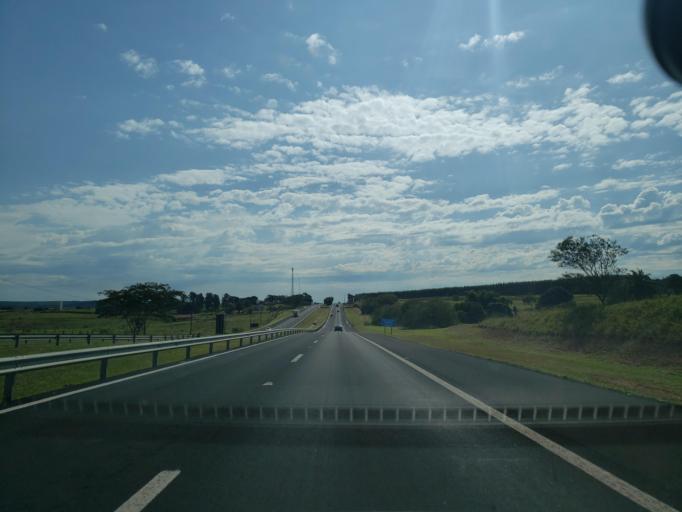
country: BR
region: Sao Paulo
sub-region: Pirajui
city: Pirajui
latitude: -22.0035
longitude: -49.4281
